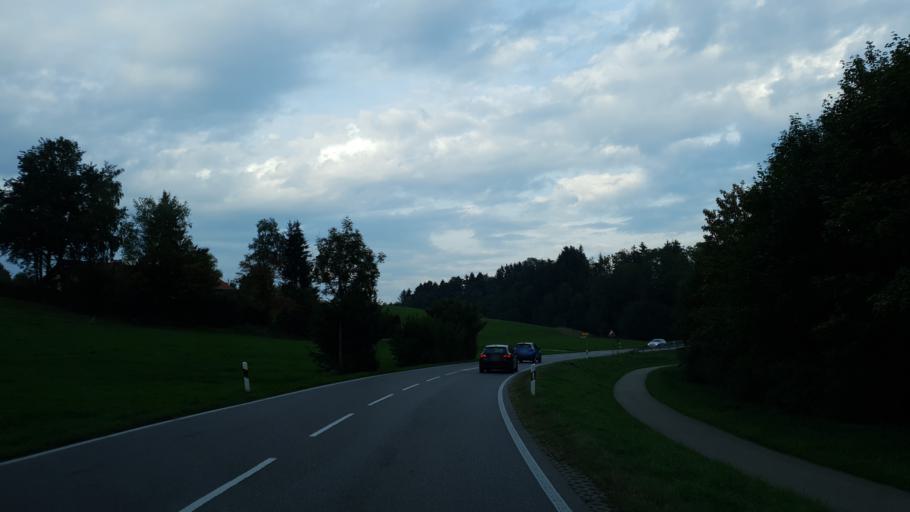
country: DE
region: Bavaria
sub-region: Swabia
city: Gestratz
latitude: 47.6647
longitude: 9.9421
